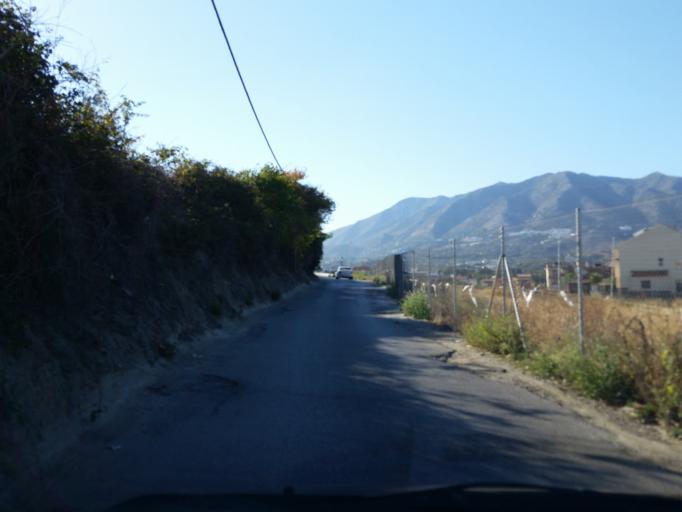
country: ES
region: Andalusia
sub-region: Provincia de Malaga
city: Fuengirola
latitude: 36.5594
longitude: -4.6212
